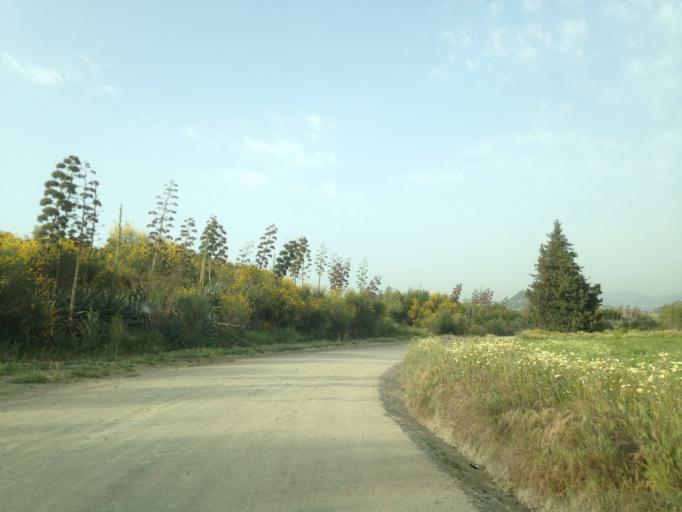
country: ES
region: Andalusia
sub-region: Provincia de Malaga
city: Estacion de Cartama
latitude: 36.7529
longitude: -4.5571
